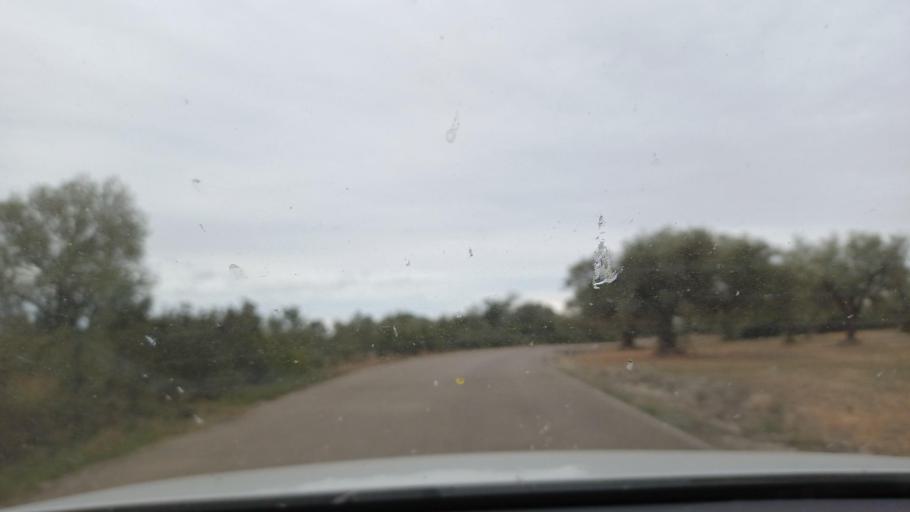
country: ES
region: Valencia
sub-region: Provincia de Castello
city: Canet lo Roig
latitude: 40.5950
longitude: 0.2834
